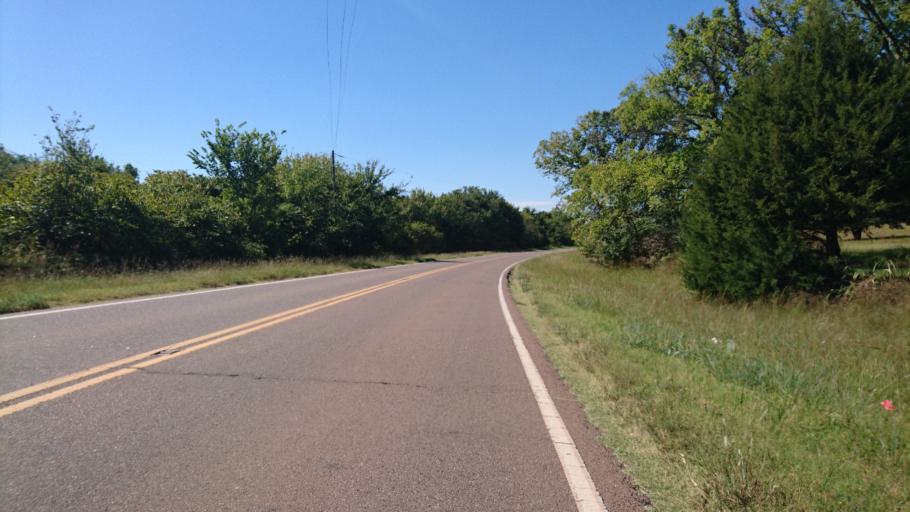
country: US
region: Oklahoma
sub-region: Oklahoma County
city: Luther
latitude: 35.6634
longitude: -97.2491
